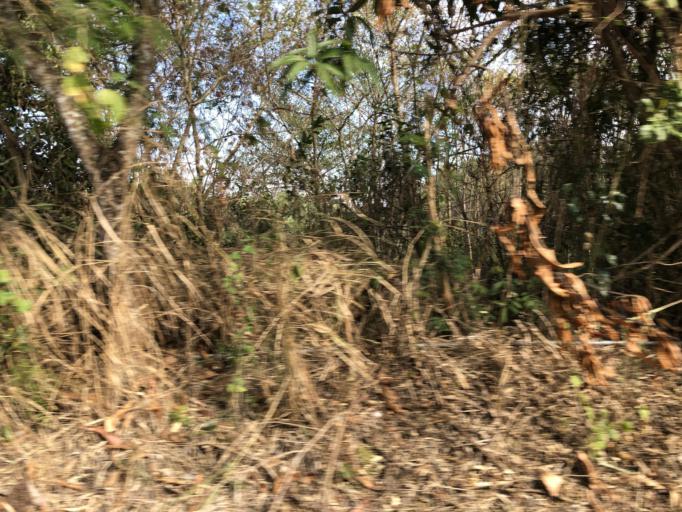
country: TW
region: Taiwan
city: Yujing
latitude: 23.0382
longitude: 120.3964
